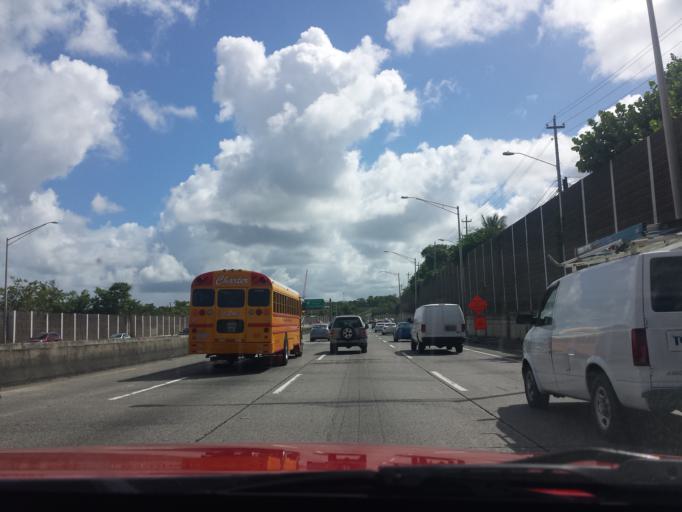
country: PR
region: Guaynabo
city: Guaynabo
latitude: 18.3968
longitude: -66.0709
